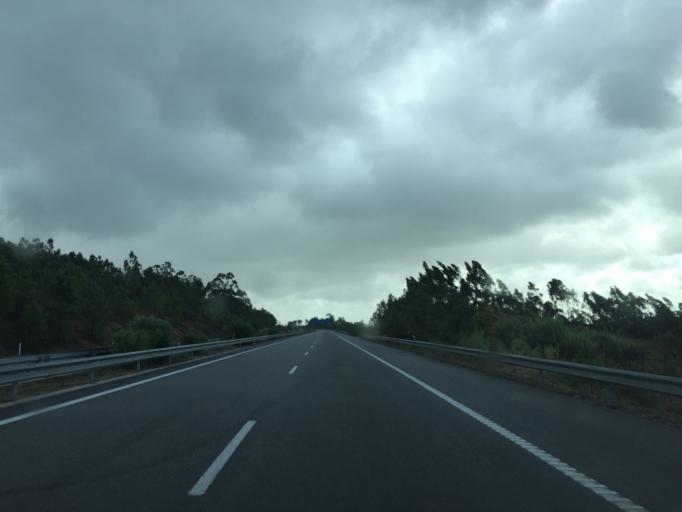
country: PT
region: Aveiro
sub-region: Mealhada
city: Pampilhosa do Botao
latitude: 40.2781
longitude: -8.5083
